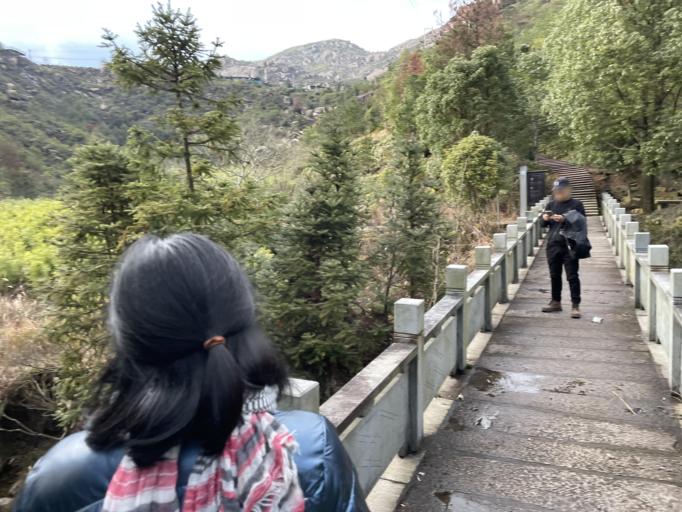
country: CN
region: Zhejiang Sheng
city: Wenzhou
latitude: 27.8778
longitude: 120.7240
